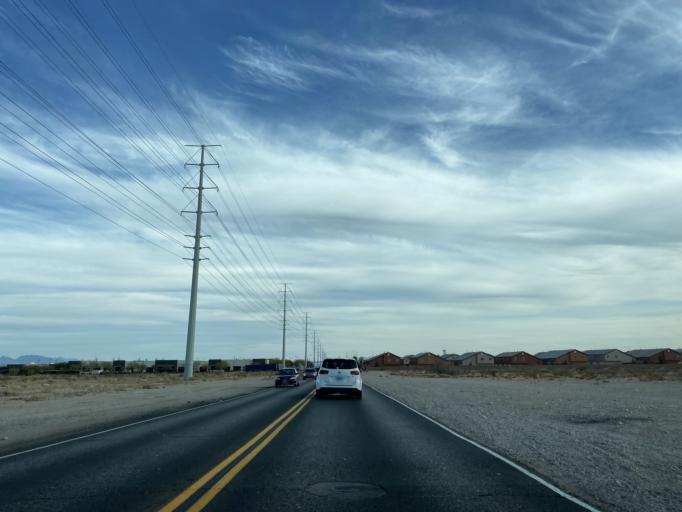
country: US
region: Nevada
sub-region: Clark County
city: Enterprise
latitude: 36.0555
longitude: -115.2571
